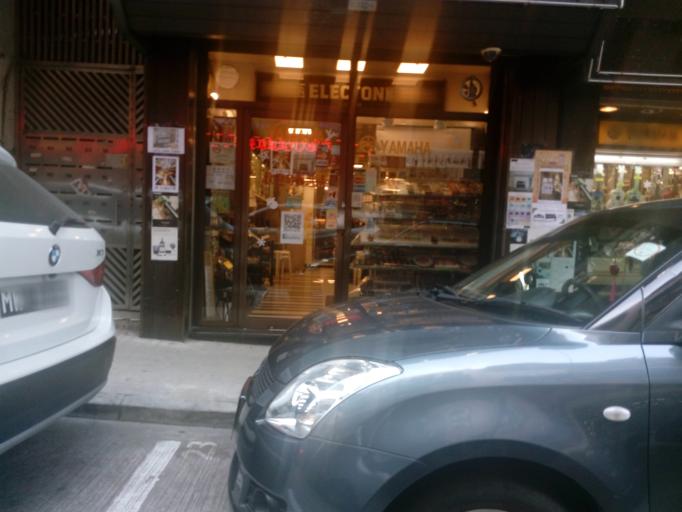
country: MO
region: Macau
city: Macau
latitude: 22.2002
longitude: 113.5459
